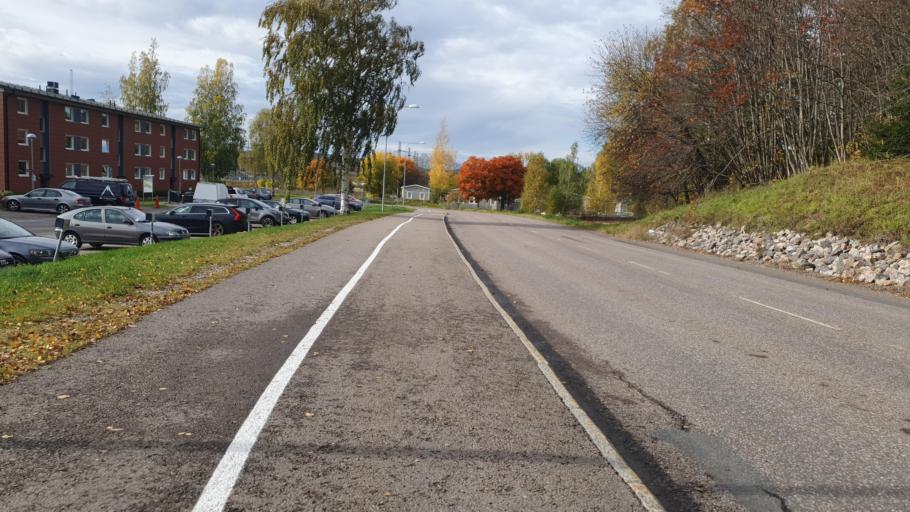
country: SE
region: Vaesternorrland
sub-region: Sundsvalls Kommun
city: Sundsvall
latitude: 62.4069
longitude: 17.2482
